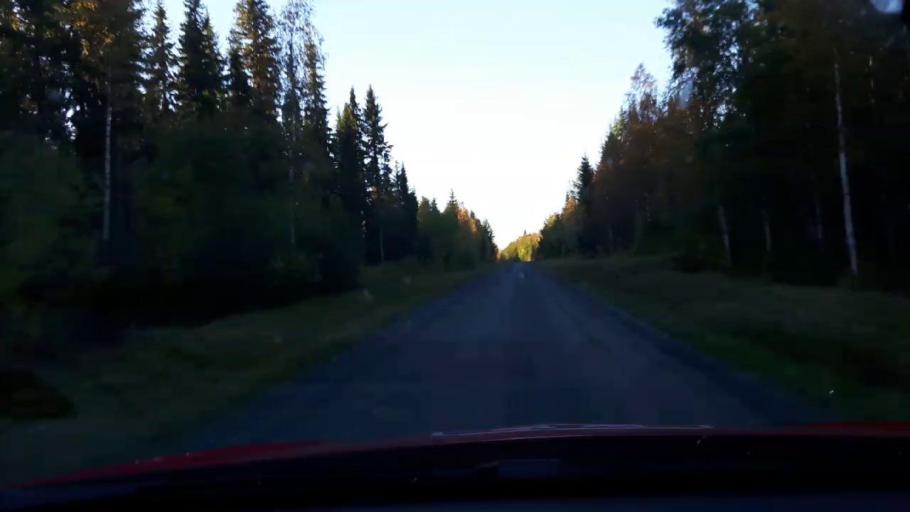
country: SE
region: Jaemtland
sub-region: Krokoms Kommun
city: Krokom
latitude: 63.4337
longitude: 14.6081
